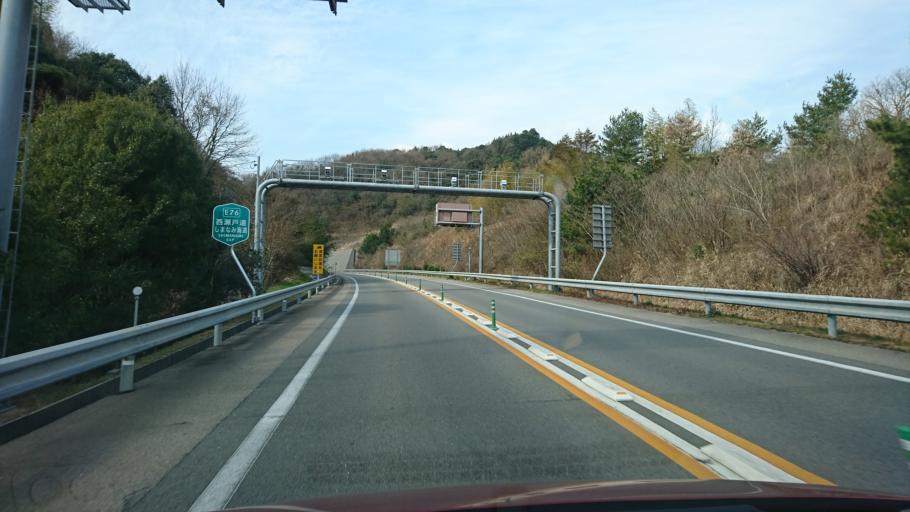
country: JP
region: Hiroshima
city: Innoshima
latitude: 34.1309
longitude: 133.0292
